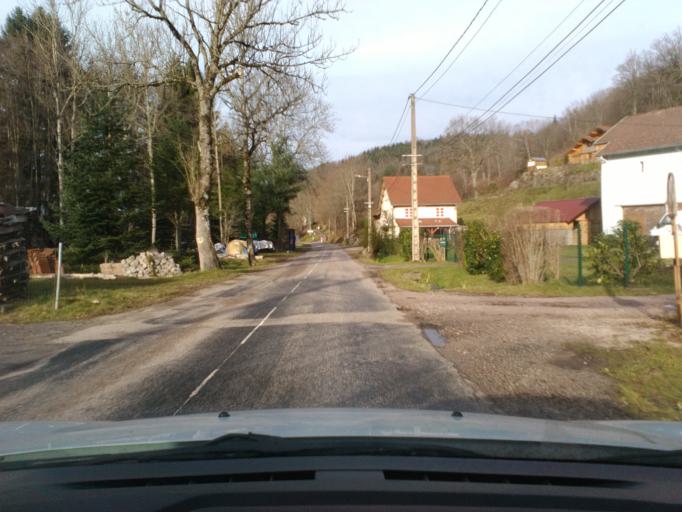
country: FR
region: Lorraine
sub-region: Departement des Vosges
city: Fraize
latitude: 48.1580
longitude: 6.9858
